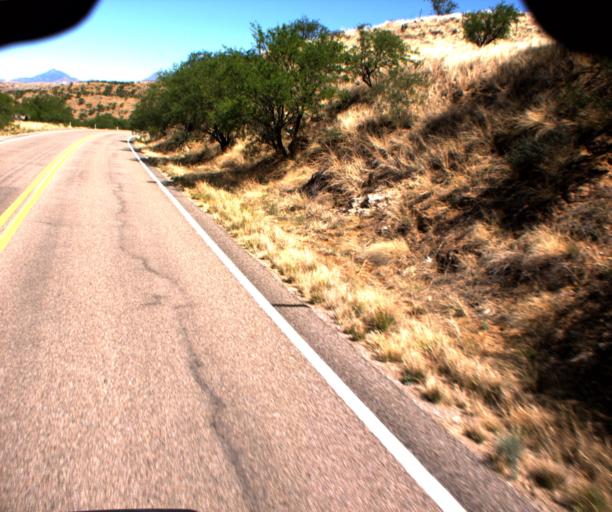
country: US
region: Arizona
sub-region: Santa Cruz County
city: Rio Rico
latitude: 31.4856
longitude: -110.8172
